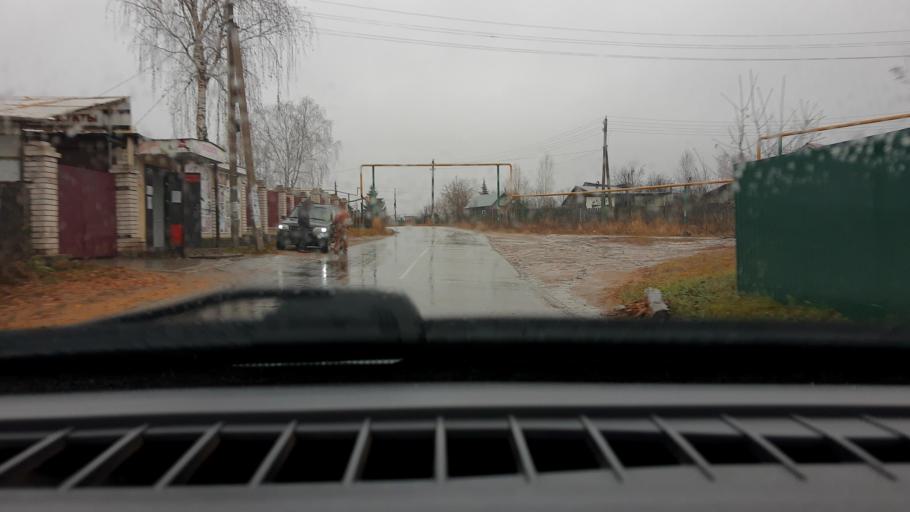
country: RU
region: Nizjnij Novgorod
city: Linda
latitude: 56.6807
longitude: 44.1960
